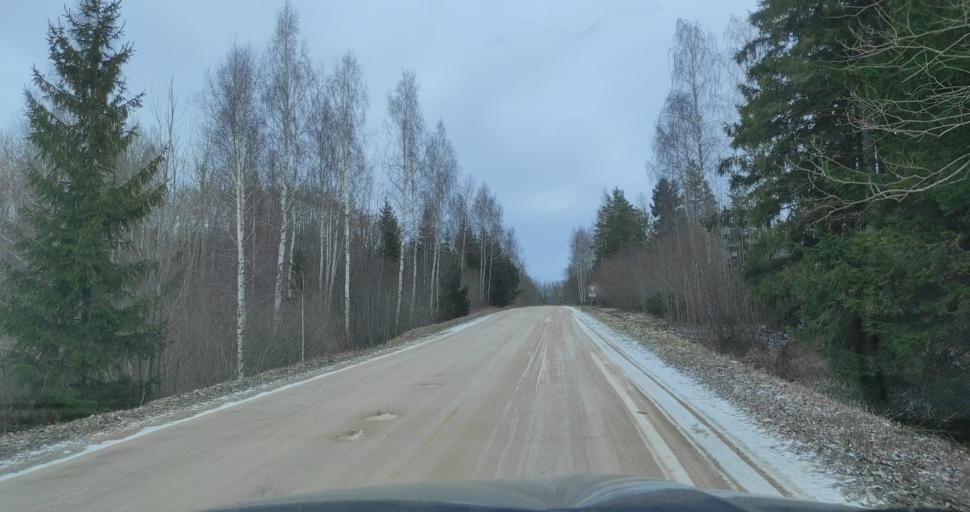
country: LV
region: Tukuma Rajons
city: Tukums
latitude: 57.0846
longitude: 23.0822
